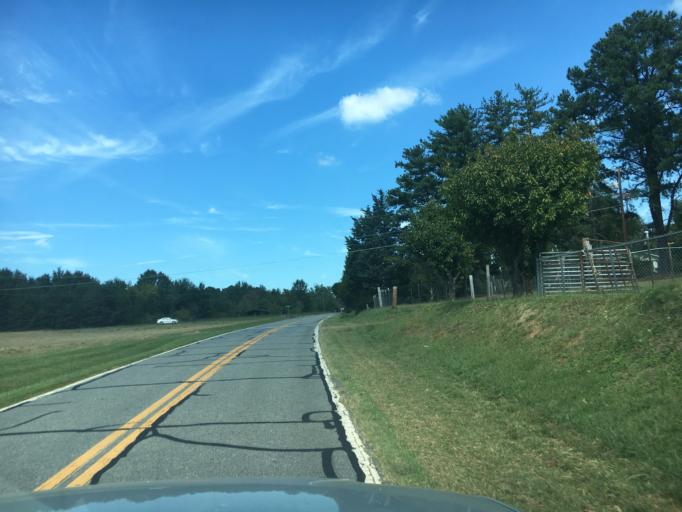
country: US
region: North Carolina
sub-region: Rutherford County
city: Spindale
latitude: 35.2642
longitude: -81.9310
